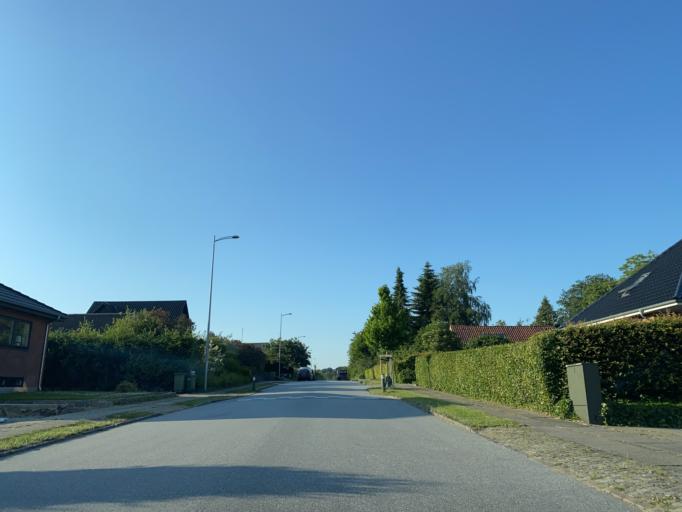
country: DK
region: South Denmark
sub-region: Aabenraa Kommune
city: Aabenraa
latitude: 55.0553
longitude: 9.4315
